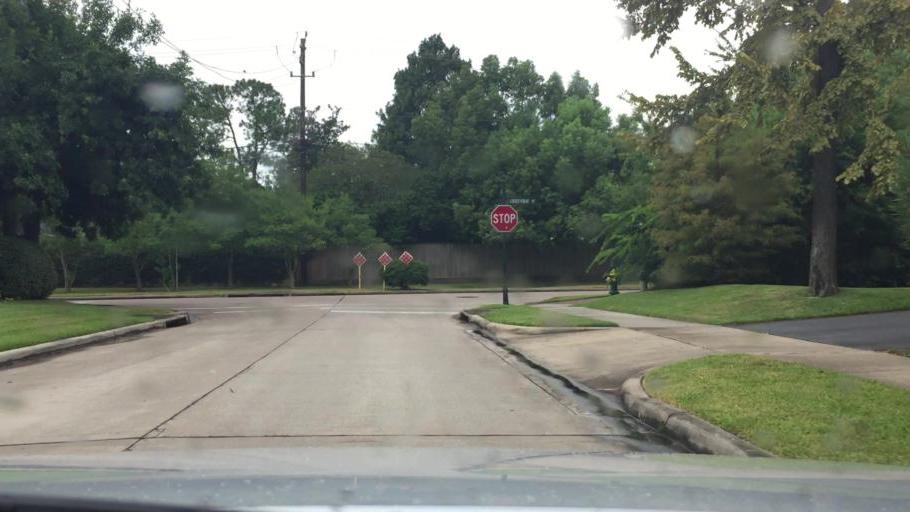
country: US
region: Texas
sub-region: Harris County
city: Piney Point Village
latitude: 29.7629
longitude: -95.5088
